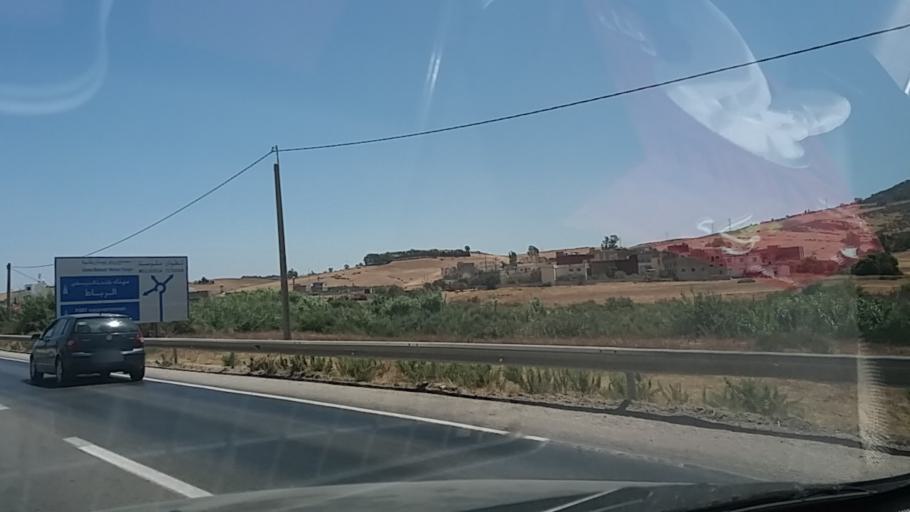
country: MA
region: Tanger-Tetouan
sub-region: Tanger-Assilah
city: Tangier
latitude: 35.6788
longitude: -5.7089
